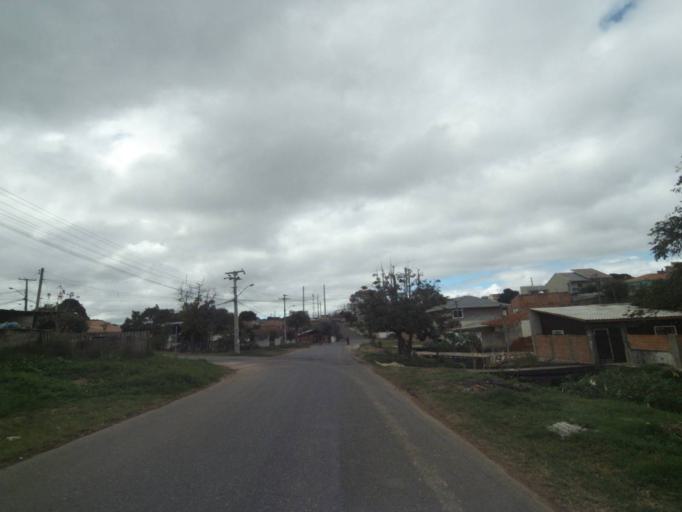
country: BR
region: Parana
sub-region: Sao Jose Dos Pinhais
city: Sao Jose dos Pinhais
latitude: -25.5384
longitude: -49.2867
